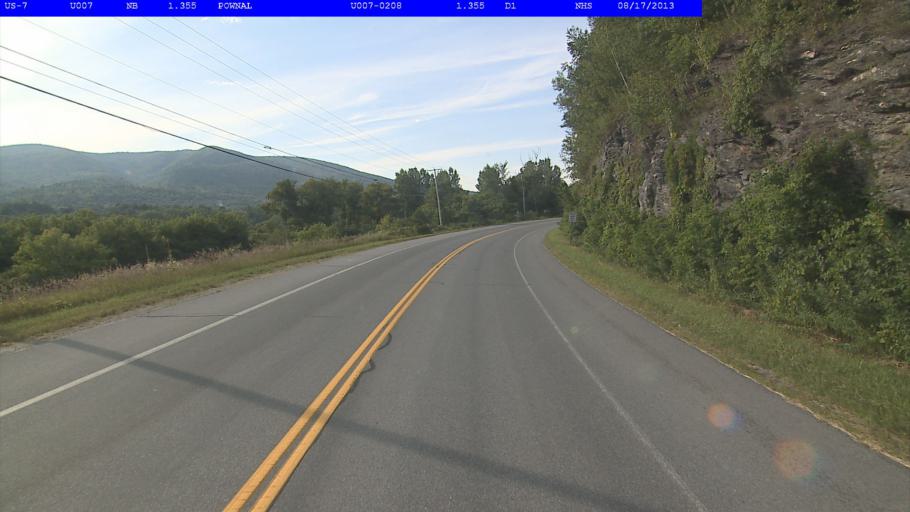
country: US
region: Massachusetts
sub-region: Berkshire County
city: Williamstown
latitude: 42.7563
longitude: -73.2308
